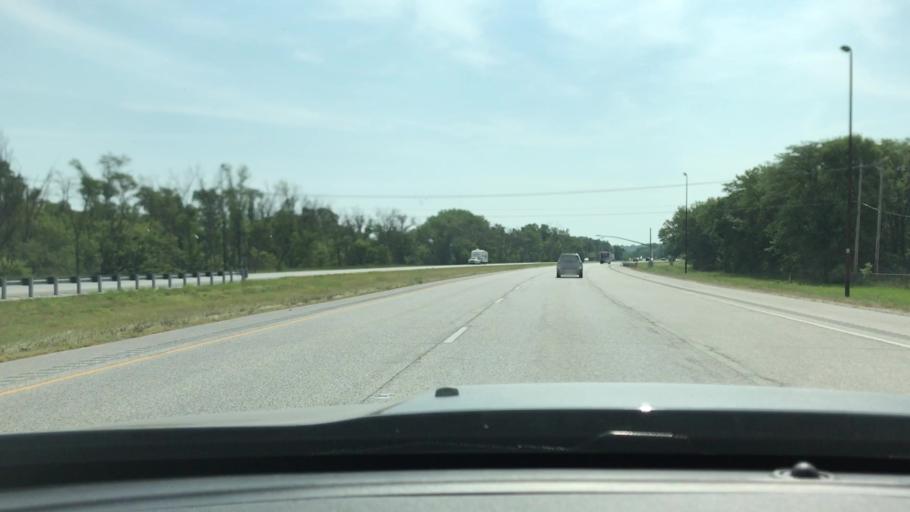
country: US
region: Illinois
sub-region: Rock Island County
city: Coal Valley
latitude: 41.4575
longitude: -90.4911
